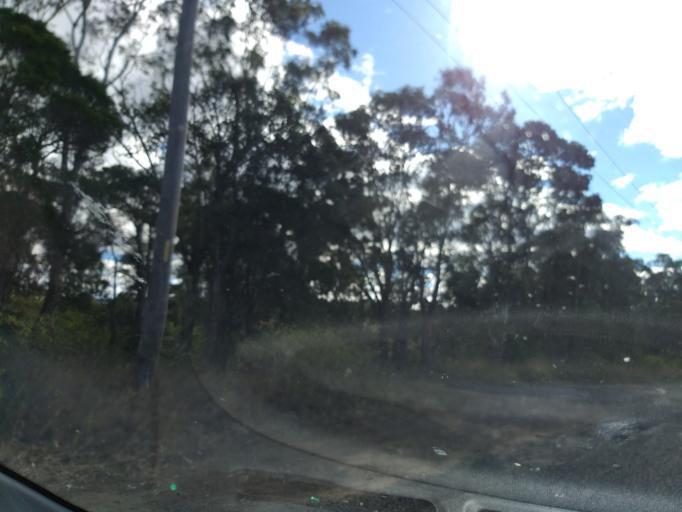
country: AU
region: New South Wales
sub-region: Shellharbour
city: Albion Park Rail
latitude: -34.5393
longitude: 150.7842
